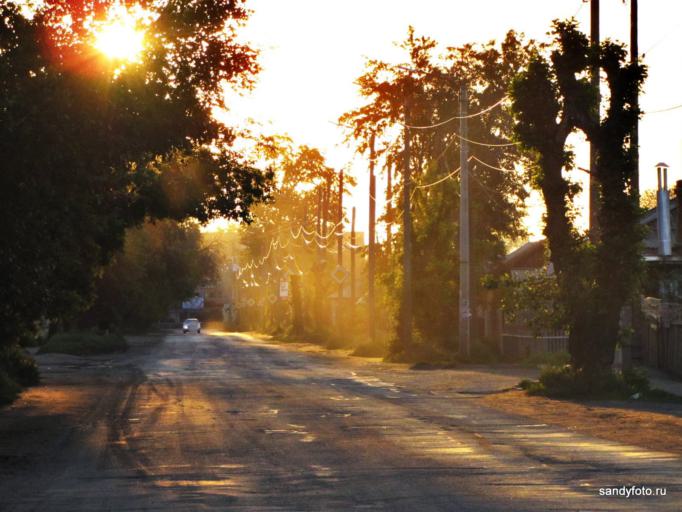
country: RU
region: Chelyabinsk
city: Troitsk
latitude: 54.0452
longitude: 61.6287
